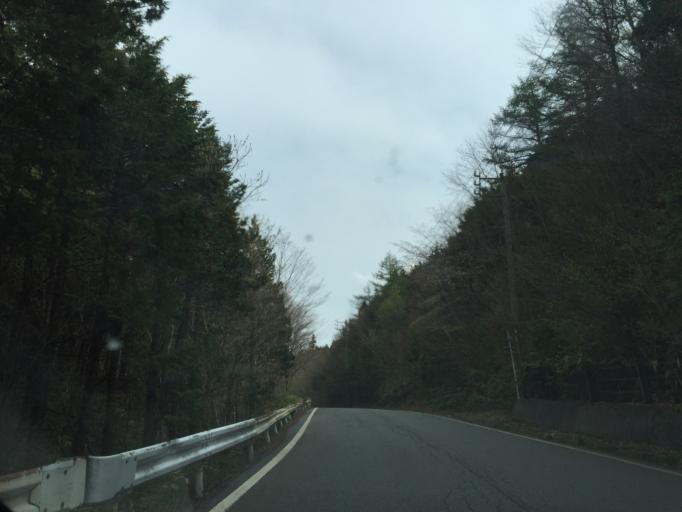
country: JP
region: Gifu
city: Nakatsugawa
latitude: 35.2993
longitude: 137.6678
